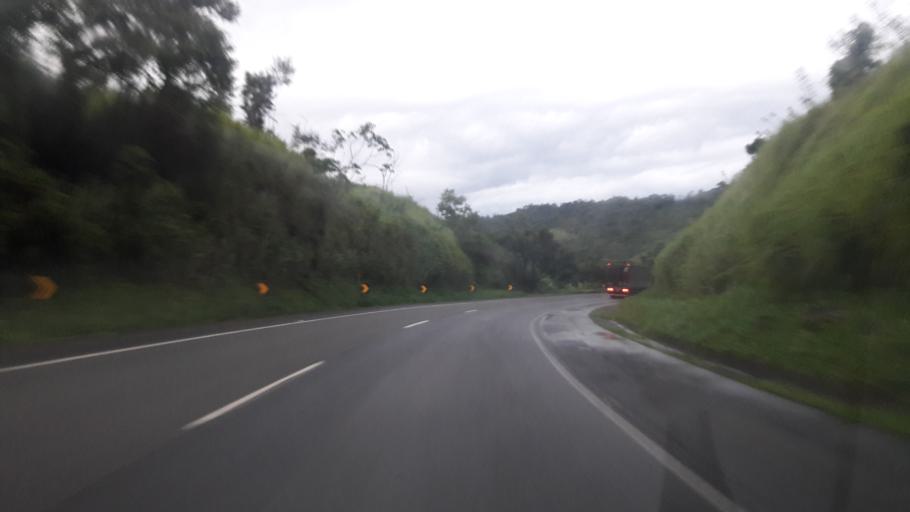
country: BR
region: Sao Paulo
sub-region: Cajati
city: Cajati
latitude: -24.7915
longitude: -48.2060
